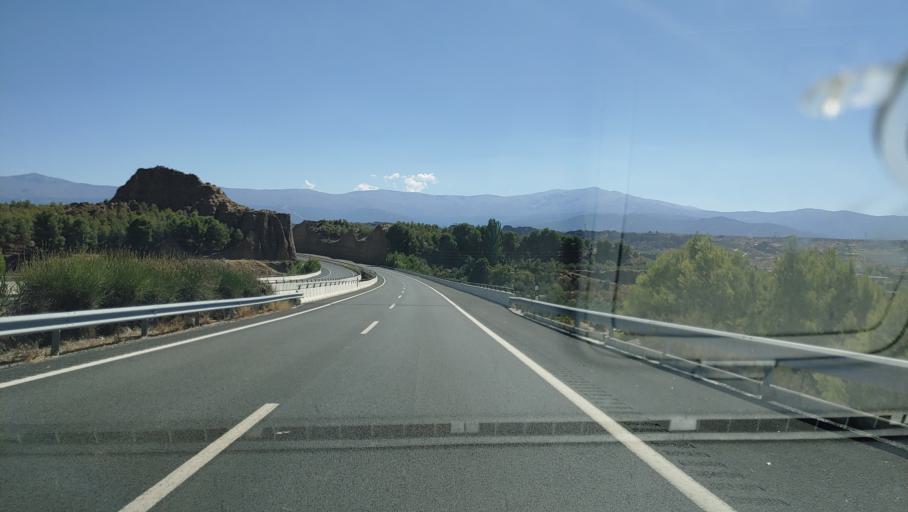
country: ES
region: Andalusia
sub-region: Provincia de Granada
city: Guadix
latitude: 37.2966
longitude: -3.1099
